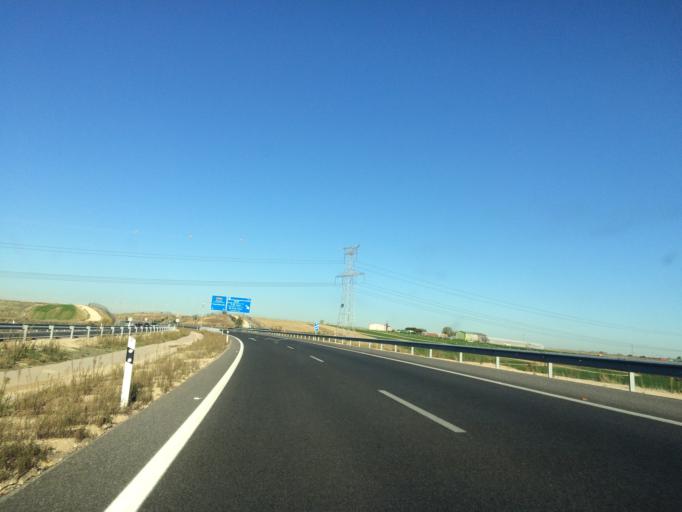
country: ES
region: Madrid
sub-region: Provincia de Madrid
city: Grinon
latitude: 40.2362
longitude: -3.8601
